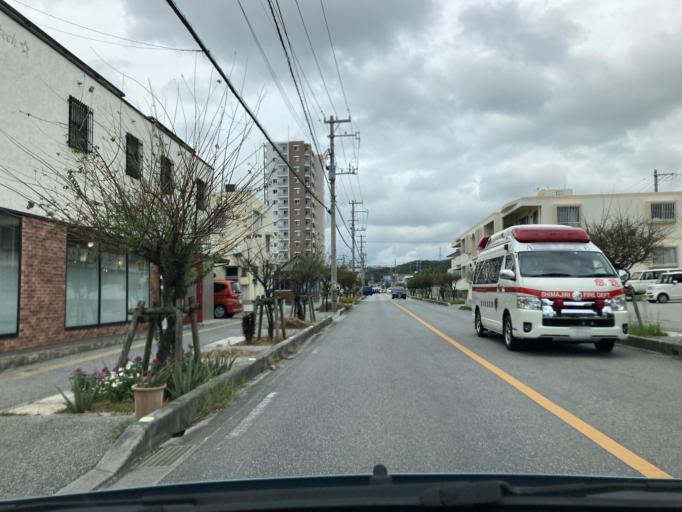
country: JP
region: Okinawa
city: Ginowan
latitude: 26.2243
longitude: 127.7683
